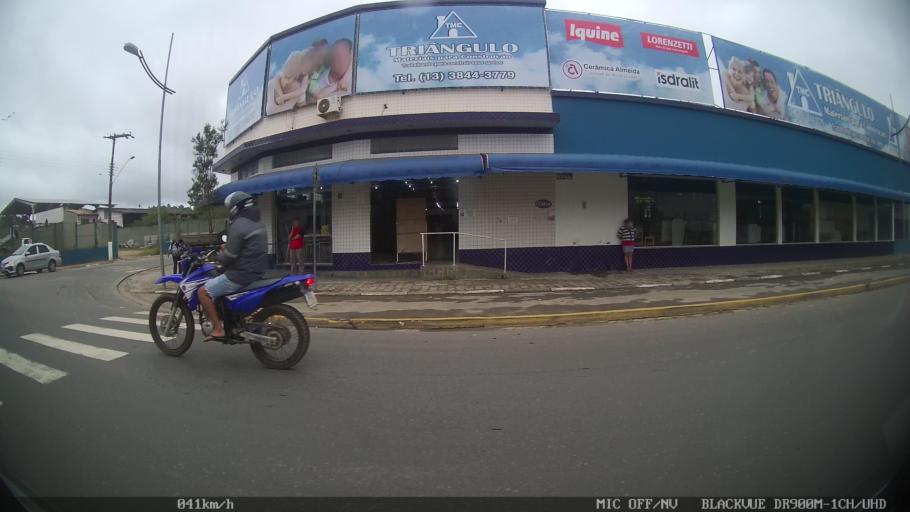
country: BR
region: Sao Paulo
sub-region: Juquia
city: Juquia
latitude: -24.3142
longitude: -47.6299
